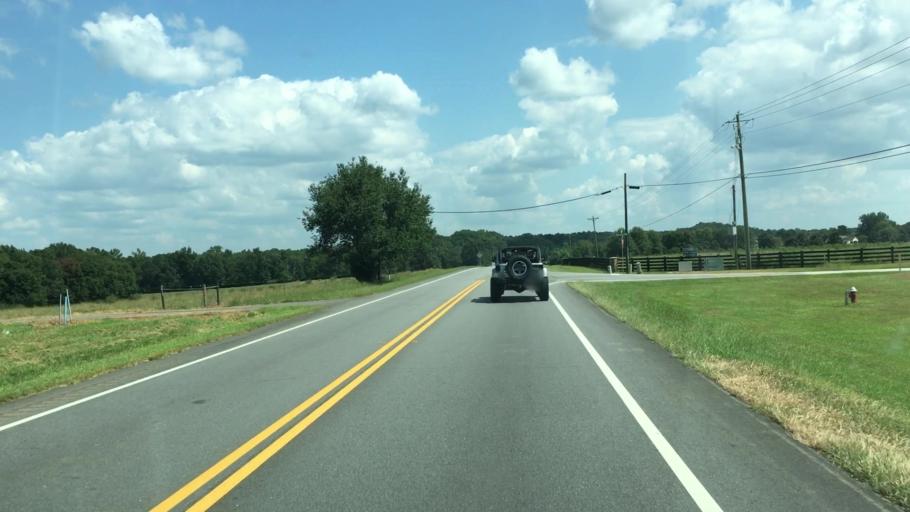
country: US
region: Georgia
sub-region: Morgan County
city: Madison
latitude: 33.5381
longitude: -83.4603
